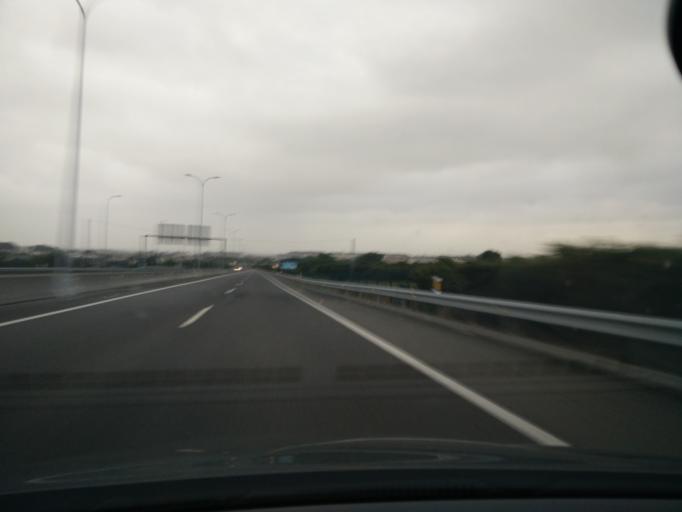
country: ES
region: Galicia
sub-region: Provincia de Lugo
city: Ribadeo
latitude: 43.5415
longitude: -7.0595
